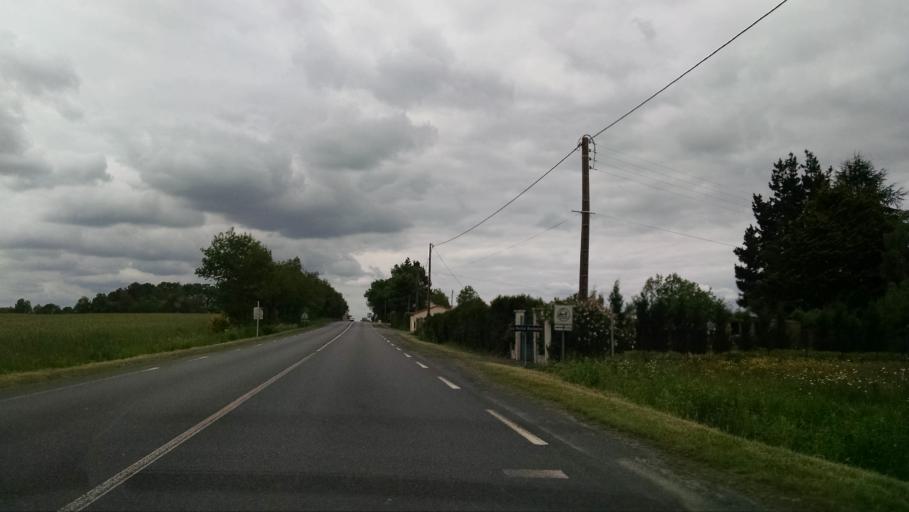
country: FR
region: Pays de la Loire
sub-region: Departement de la Loire-Atlantique
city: Aigrefeuille-sur-Maine
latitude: 47.0933
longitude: -1.4416
